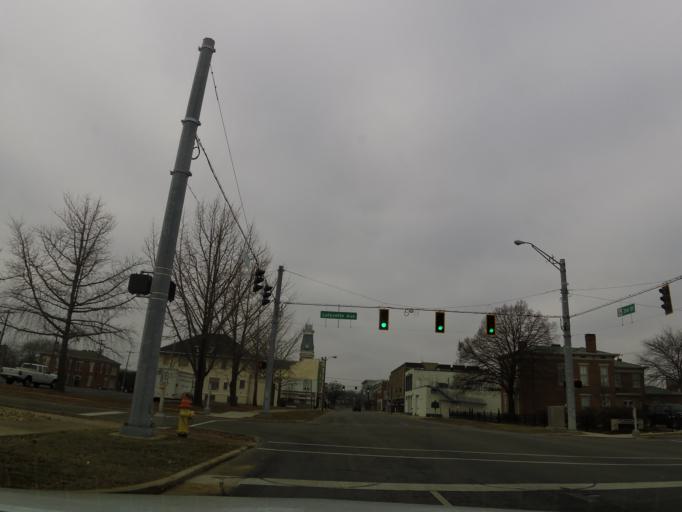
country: US
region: Indiana
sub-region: Bartholomew County
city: Columbus
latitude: 39.2015
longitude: -85.9181
